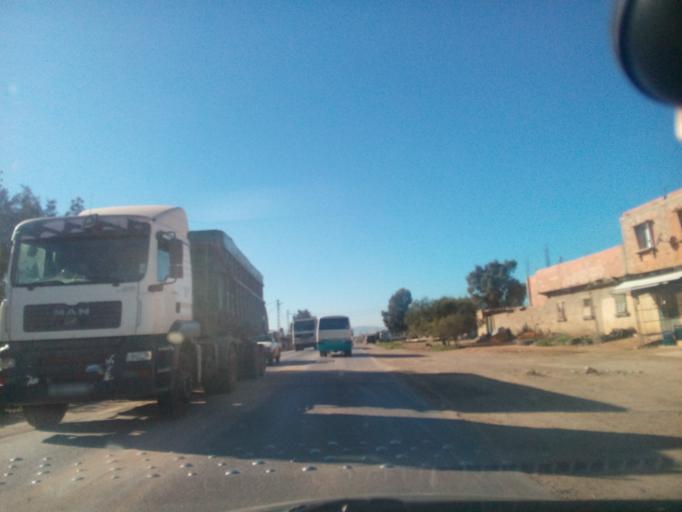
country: DZ
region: Relizane
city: Djidiouia
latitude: 35.8948
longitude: 0.6663
